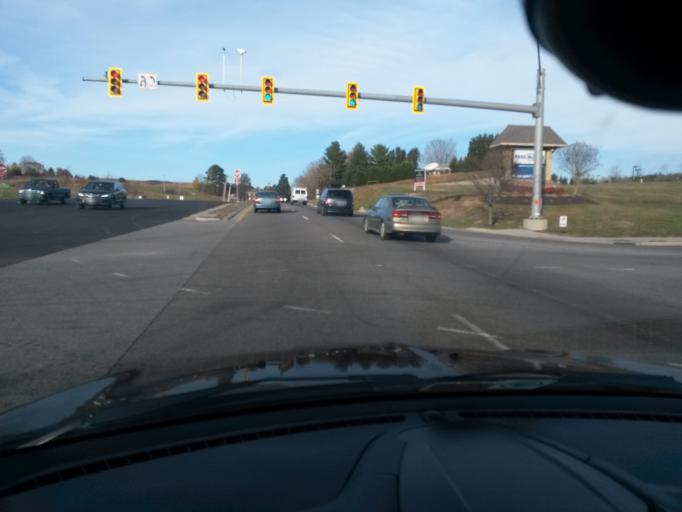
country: US
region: Virginia
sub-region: Botetourt County
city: Daleville
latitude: 37.4168
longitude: -79.9119
